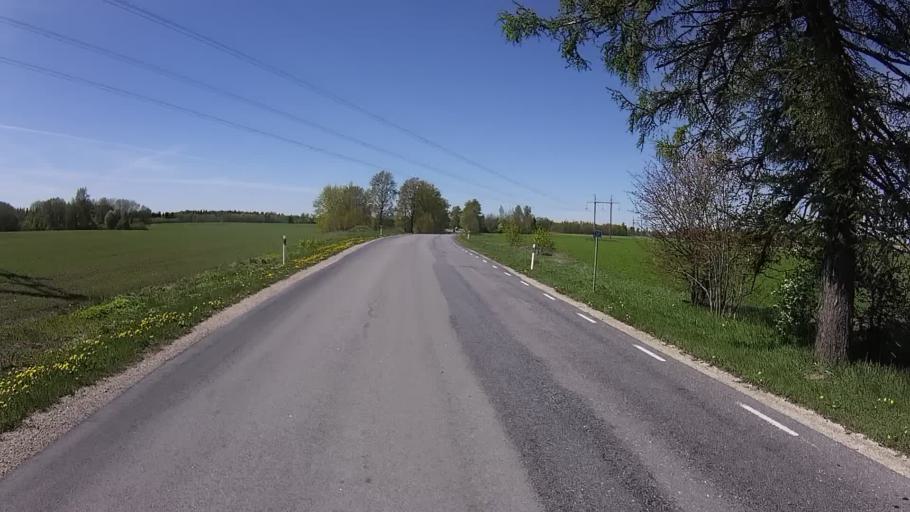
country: EE
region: Raplamaa
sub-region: Kehtna vald
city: Kehtna
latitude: 59.0544
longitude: 24.9957
